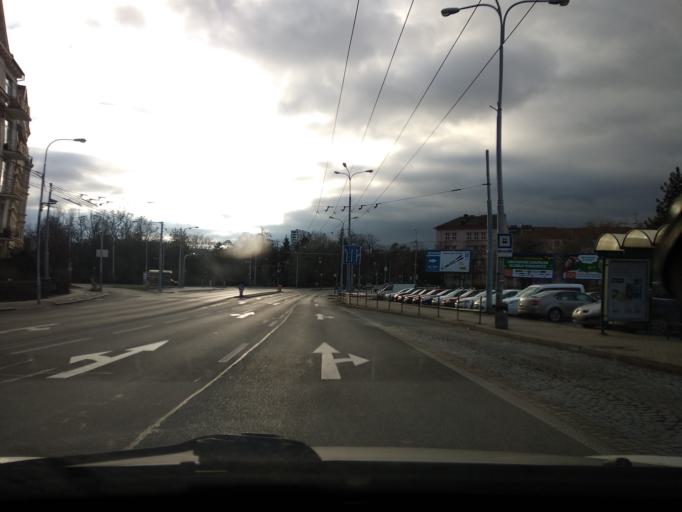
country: CZ
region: South Moravian
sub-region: Mesto Brno
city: Brno
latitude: 49.2102
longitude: 16.6099
